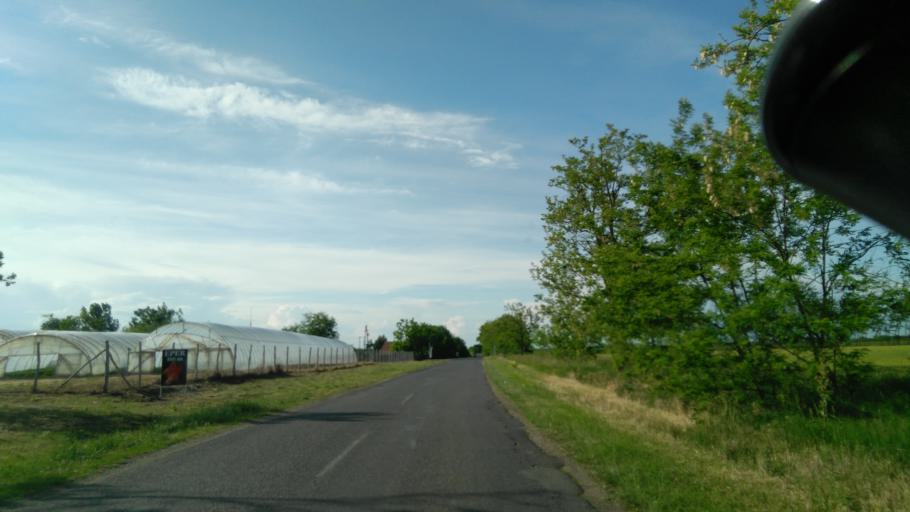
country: HU
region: Bekes
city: Lokoshaza
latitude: 46.4644
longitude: 21.2084
